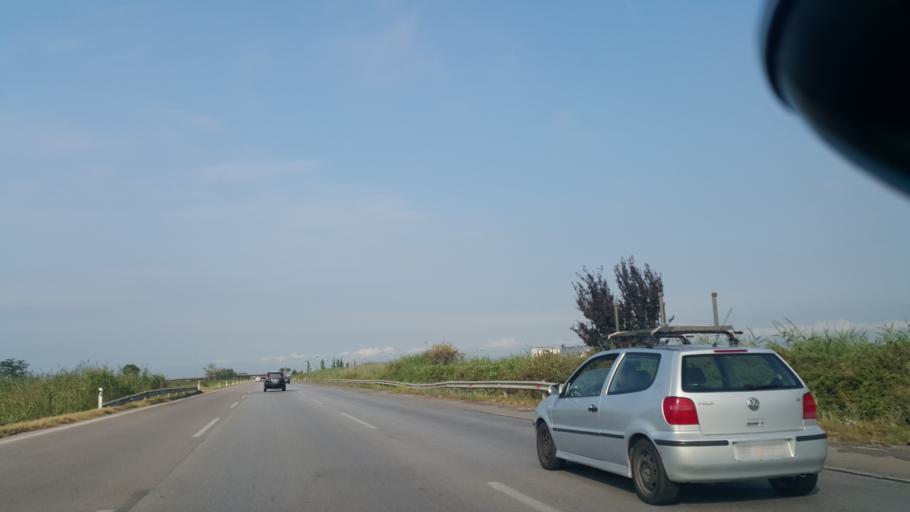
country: GR
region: Central Macedonia
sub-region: Nomos Thessalonikis
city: Chalastra
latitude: 40.6182
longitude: 22.7507
